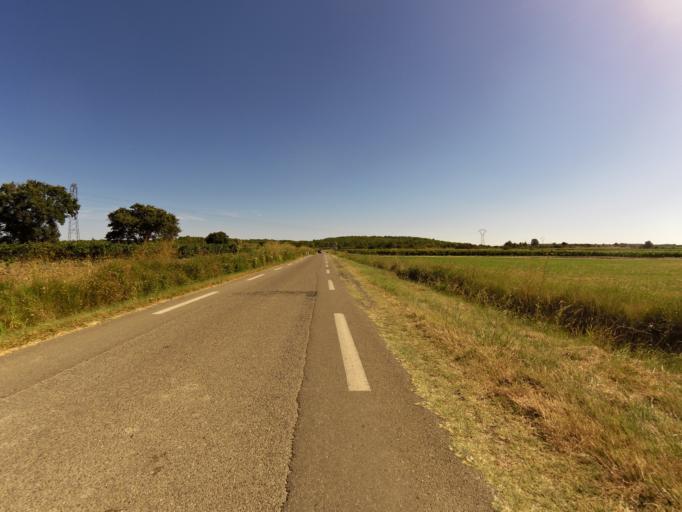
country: FR
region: Languedoc-Roussillon
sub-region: Departement du Gard
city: Aigues-Vives
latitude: 43.7474
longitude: 4.1832
